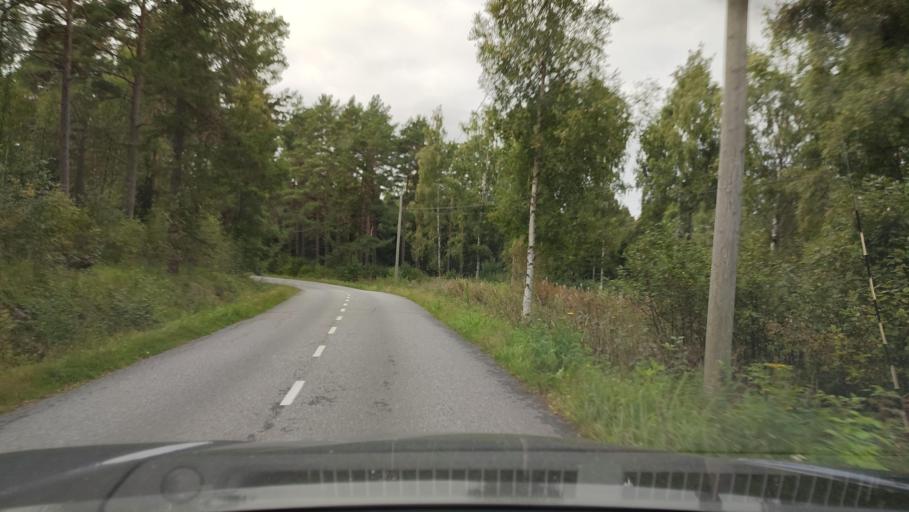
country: FI
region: Ostrobothnia
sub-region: Sydosterbotten
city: Kristinestad
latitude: 62.2762
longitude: 21.3560
